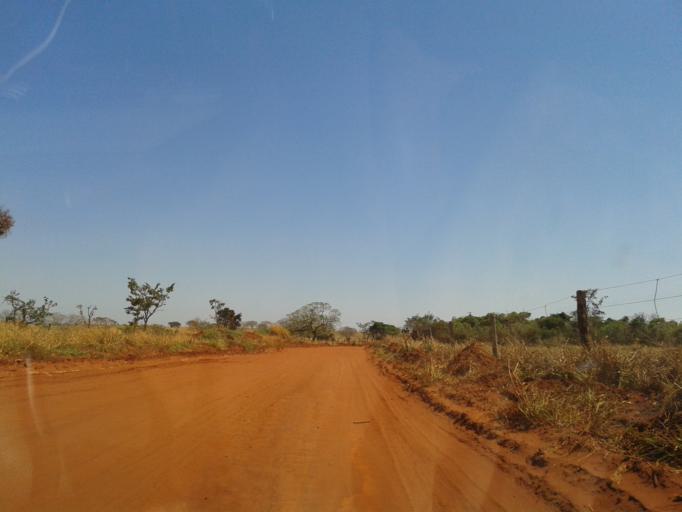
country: BR
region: Minas Gerais
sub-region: Ituiutaba
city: Ituiutaba
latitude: -18.9907
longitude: -49.3845
